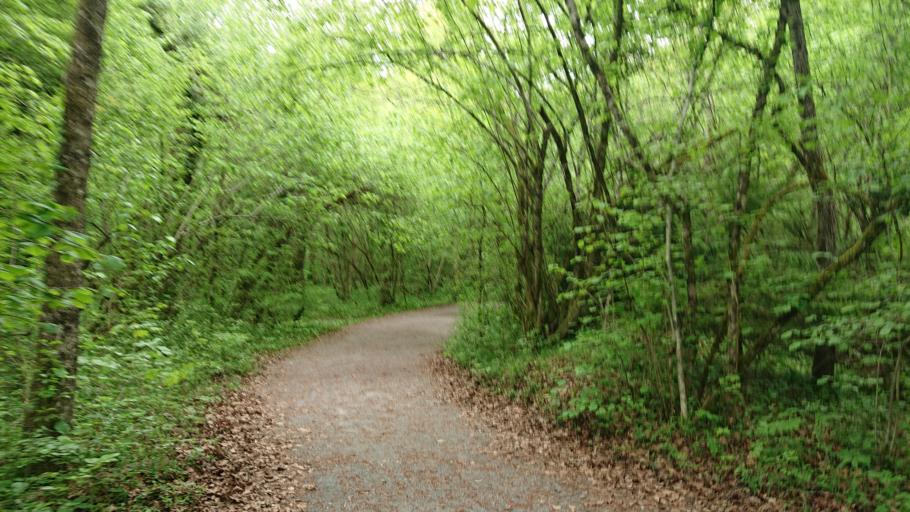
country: FR
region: Rhone-Alpes
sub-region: Departement de la Haute-Savoie
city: Doussard
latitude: 45.7873
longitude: 6.2257
